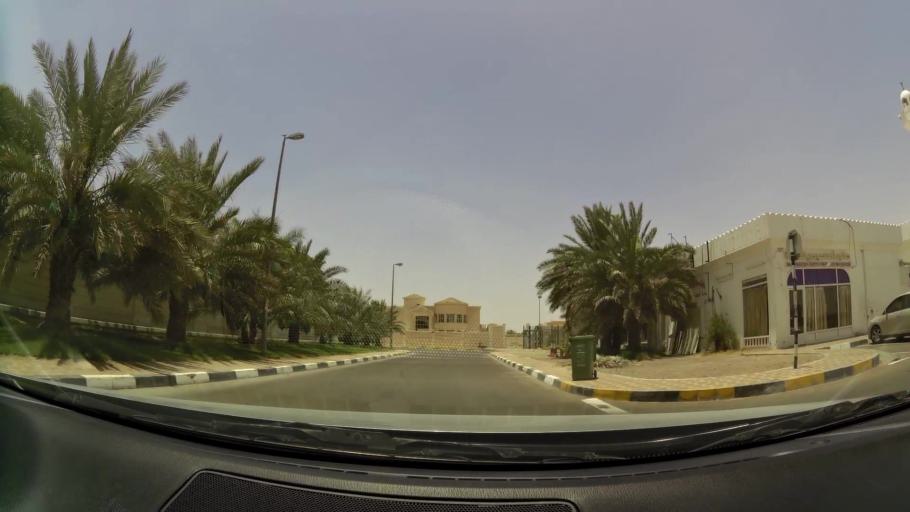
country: OM
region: Al Buraimi
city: Al Buraymi
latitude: 24.2808
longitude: 55.7323
